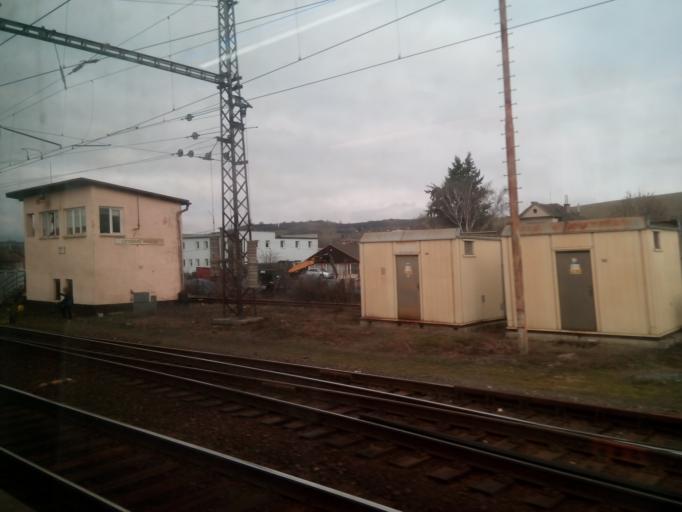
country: SK
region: Zilinsky
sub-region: Okres Liptovsky Mikulas
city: Liptovsky Mikulas
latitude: 49.0911
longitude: 19.6109
